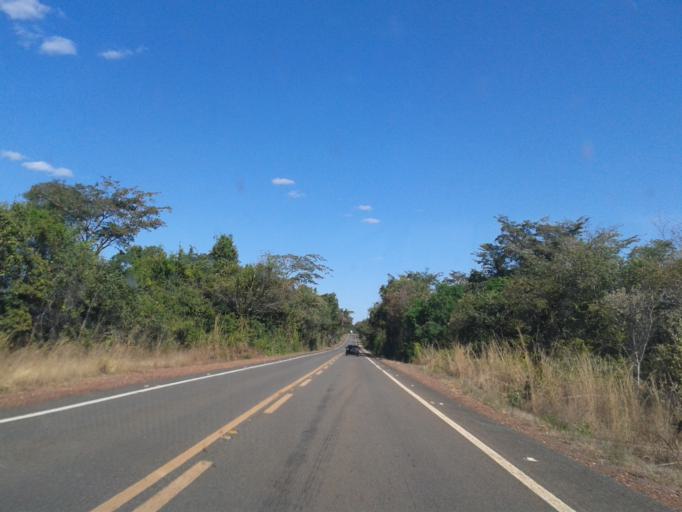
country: BR
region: Goias
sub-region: Sao Miguel Do Araguaia
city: Sao Miguel do Araguaia
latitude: -13.8602
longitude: -50.3344
